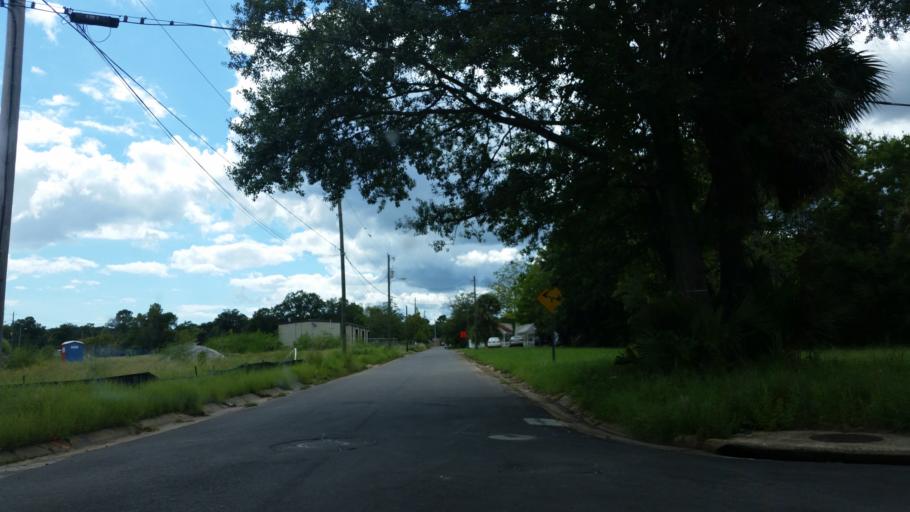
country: US
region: Florida
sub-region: Escambia County
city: Pensacola
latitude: 30.4090
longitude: -87.2226
